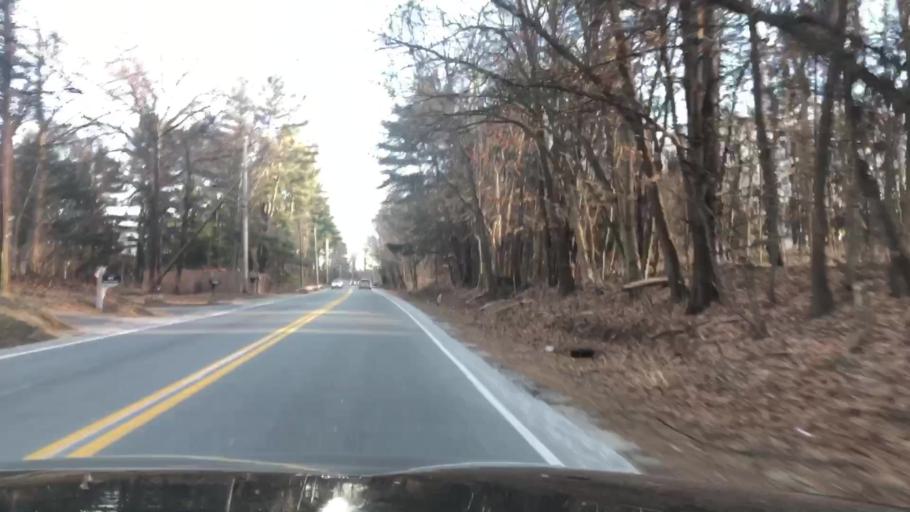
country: US
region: Massachusetts
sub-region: Worcester County
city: Bolton
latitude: 42.4441
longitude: -71.6234
